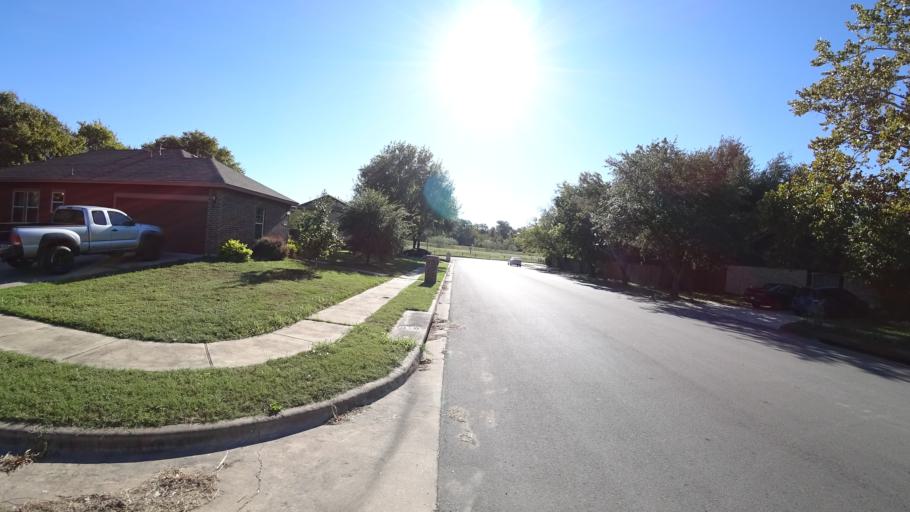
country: US
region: Texas
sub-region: Travis County
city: Hornsby Bend
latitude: 30.3124
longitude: -97.6512
